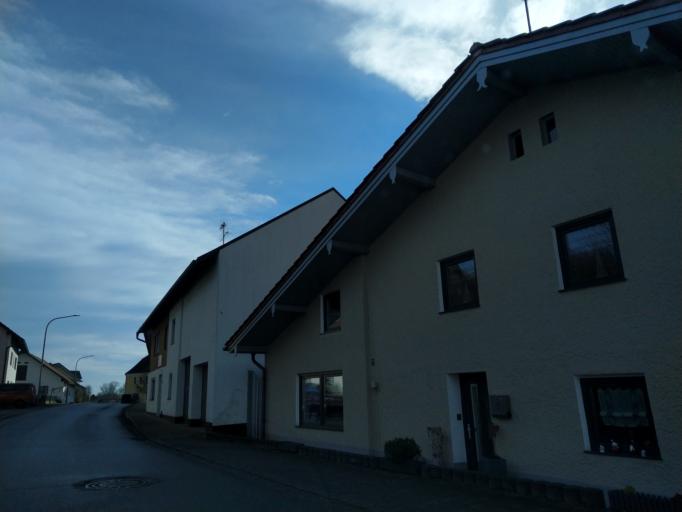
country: DE
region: Bavaria
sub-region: Lower Bavaria
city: Rossbach
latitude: 48.6243
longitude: 12.9604
